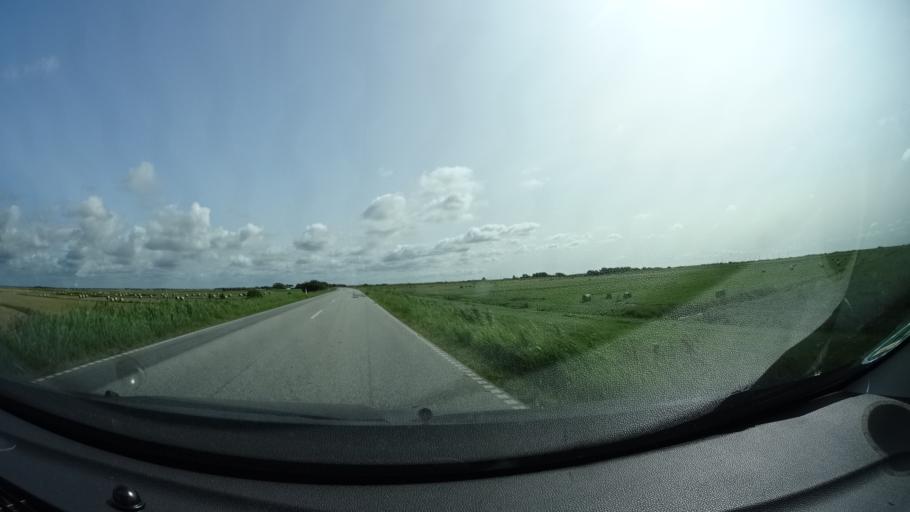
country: DE
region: Schleswig-Holstein
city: Rodenas
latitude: 54.9358
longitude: 8.7145
